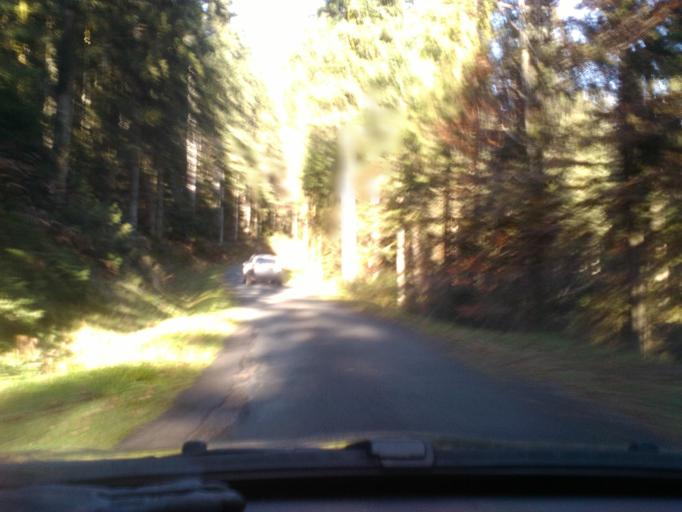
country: FR
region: Lorraine
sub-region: Departement des Vosges
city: Senones
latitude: 48.4691
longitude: 7.0745
